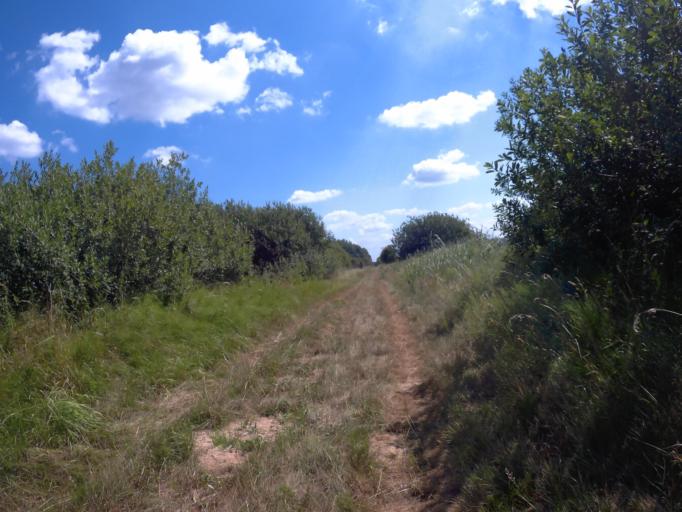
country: DE
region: Schleswig-Holstein
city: Hude
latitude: 54.3782
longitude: 9.2097
